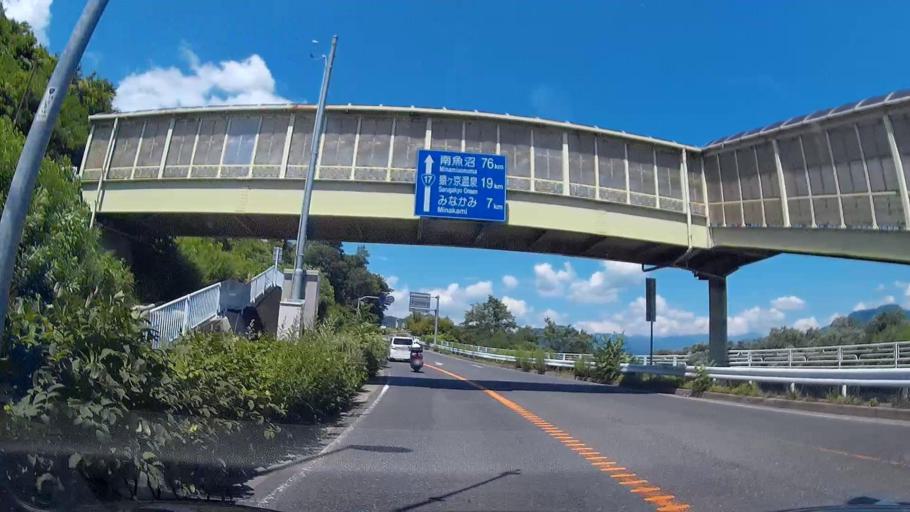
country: JP
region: Gunma
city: Numata
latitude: 36.6320
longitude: 139.0366
